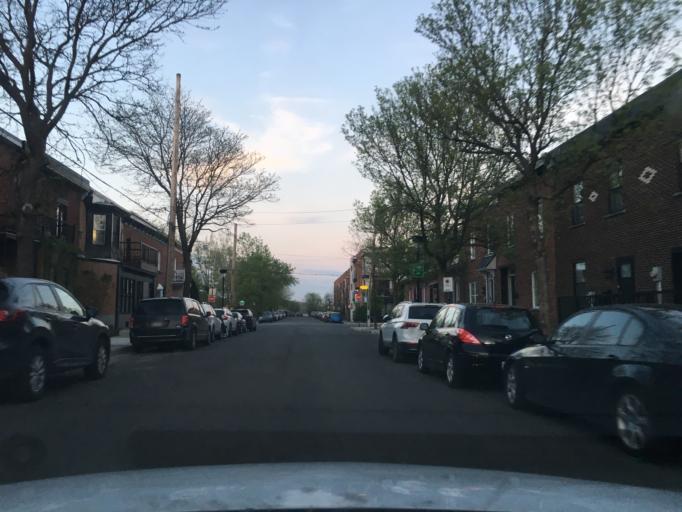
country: CA
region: Quebec
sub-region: Montreal
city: Montreal
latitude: 45.4806
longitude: -73.5541
